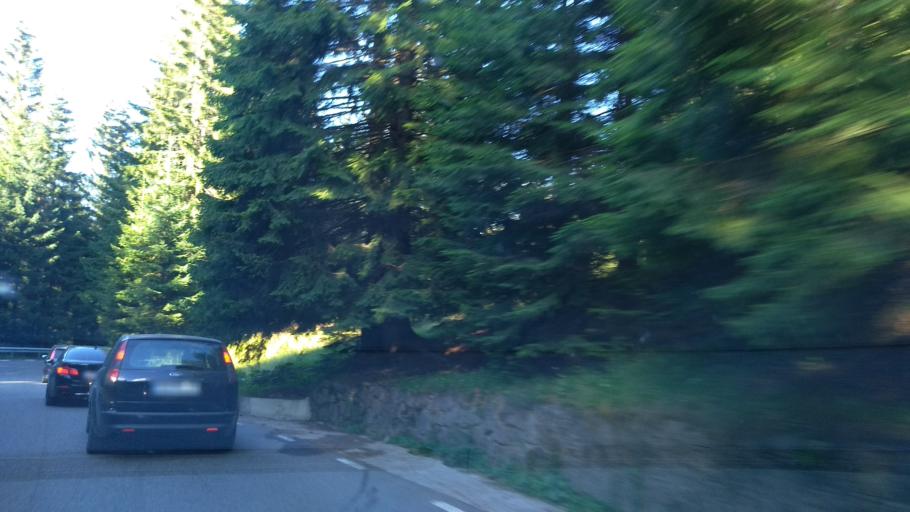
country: RO
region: Prahova
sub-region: Oras Sinaia
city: Sinaia
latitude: 45.3181
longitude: 25.4910
